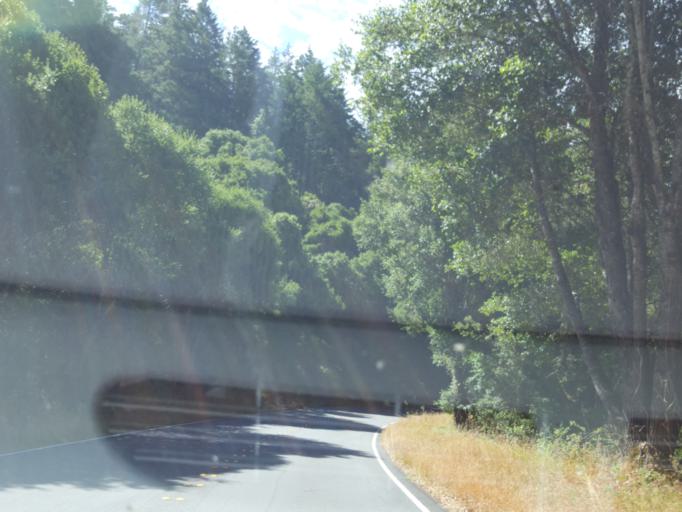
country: US
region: California
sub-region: San Mateo County
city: Portola Valley
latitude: 37.2918
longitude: -122.2789
